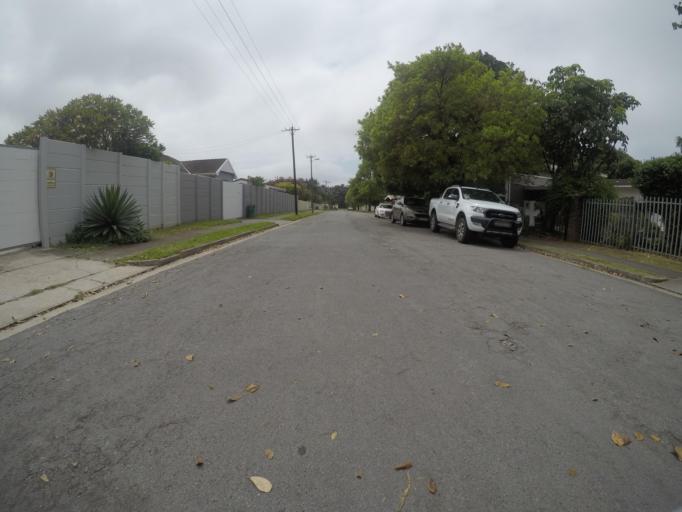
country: ZA
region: Eastern Cape
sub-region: Buffalo City Metropolitan Municipality
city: East London
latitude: -32.9888
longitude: 27.9214
